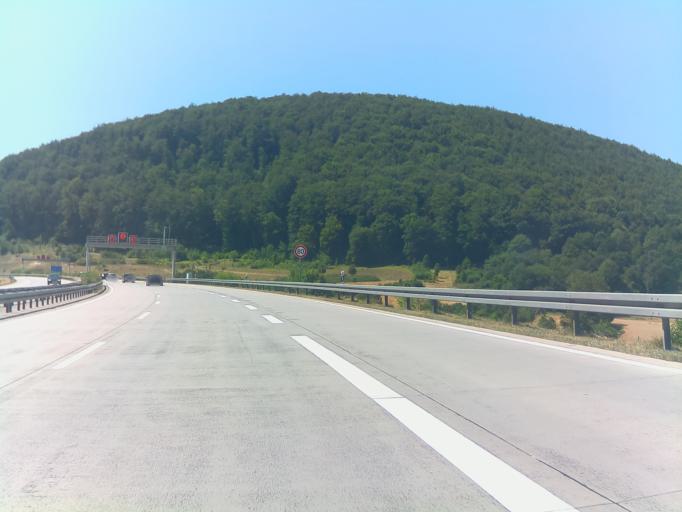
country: DE
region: Thuringia
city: Einhausen
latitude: 50.5202
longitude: 10.4620
